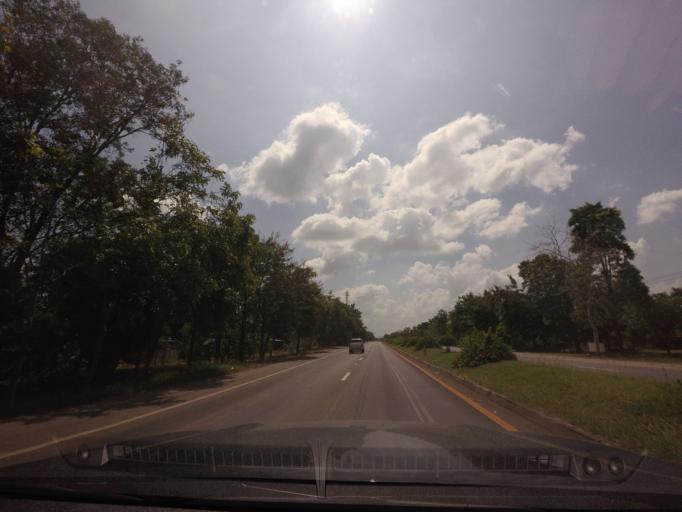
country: TH
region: Phetchabun
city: Nong Phai
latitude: 16.1378
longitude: 101.0503
